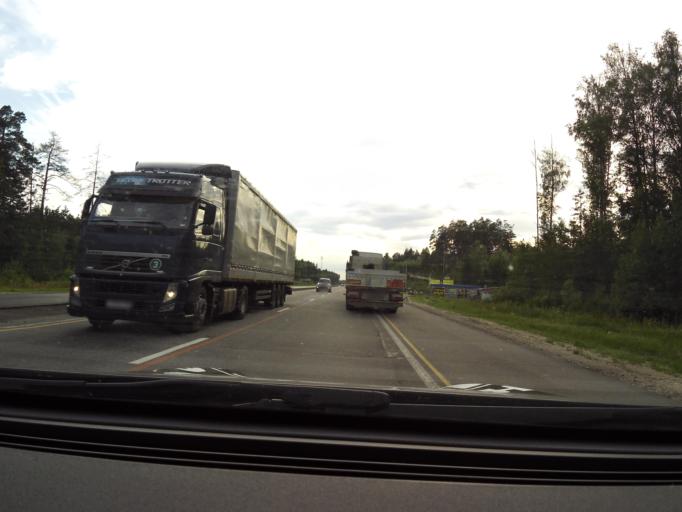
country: RU
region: Vladimir
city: Orgtrud
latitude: 56.1031
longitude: 40.7135
